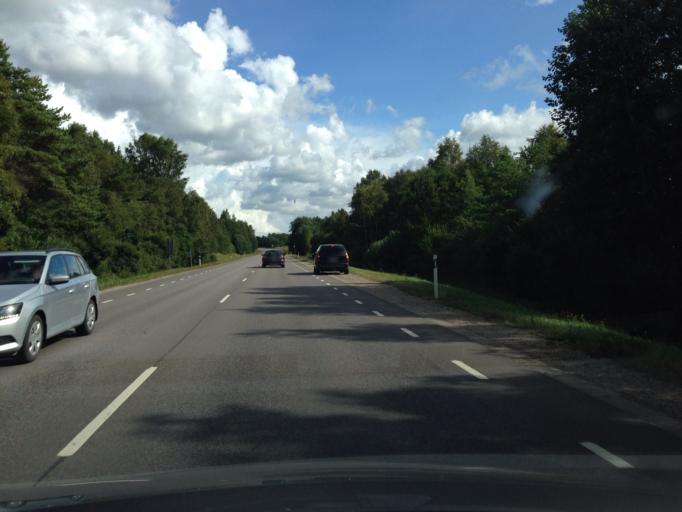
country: EE
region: Harju
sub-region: Saue vald
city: Laagri
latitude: 59.3125
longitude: 24.5954
